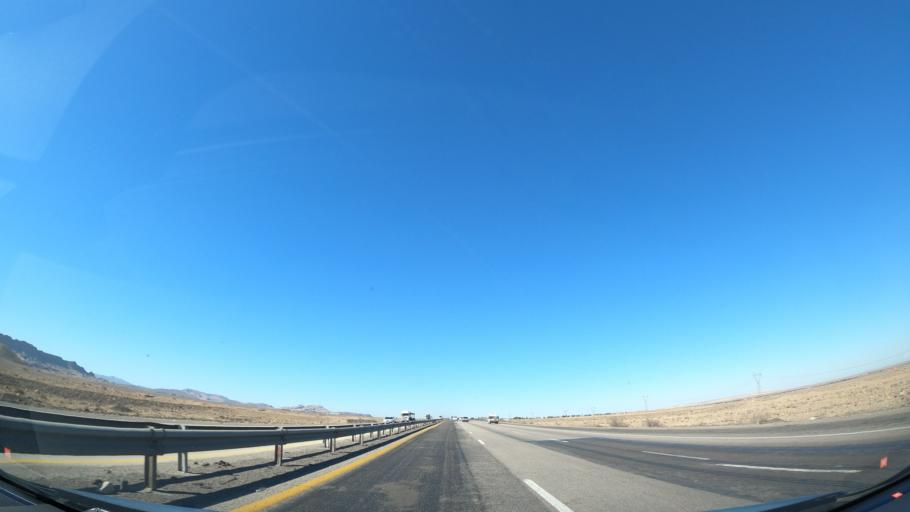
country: IR
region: Isfahan
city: Aran Bidgol
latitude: 34.3592
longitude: 51.2507
